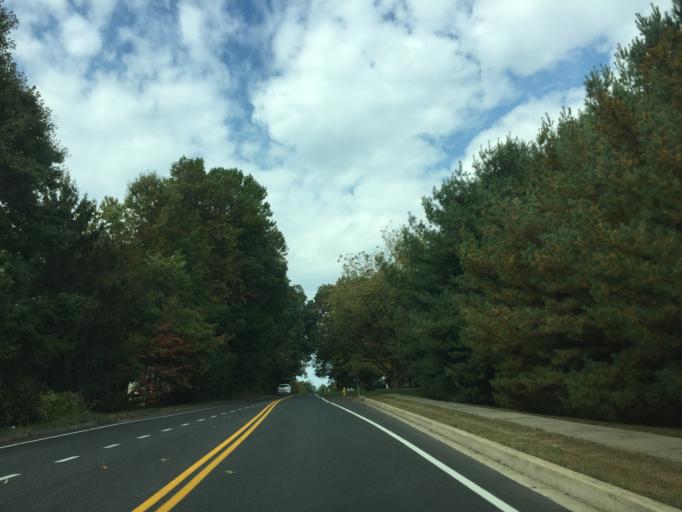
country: US
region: Maryland
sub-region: Harford County
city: Bel Air South
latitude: 39.4875
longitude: -76.3052
